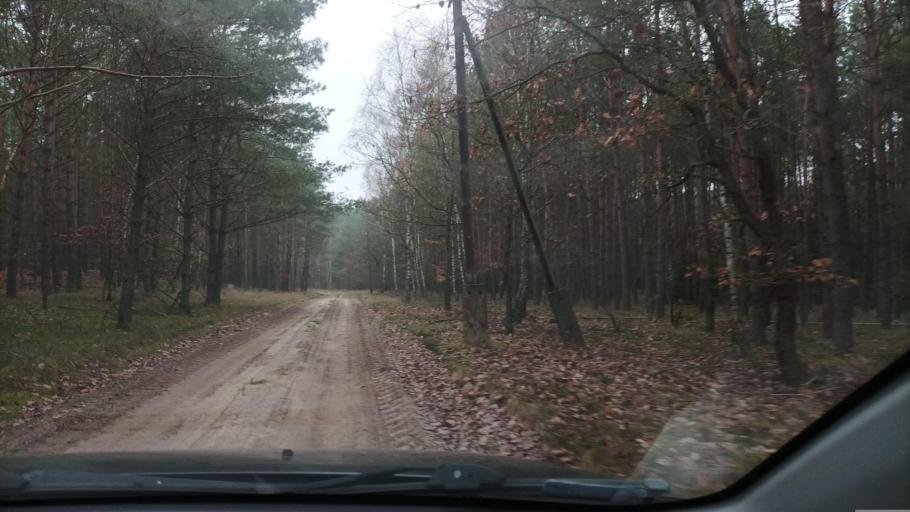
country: PL
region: Greater Poland Voivodeship
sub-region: Powiat czarnkowsko-trzcianecki
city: Polajewo
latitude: 52.7508
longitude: 16.7758
